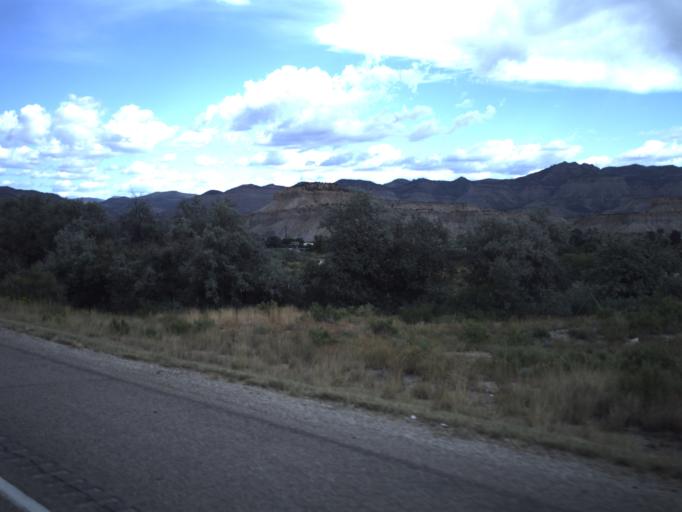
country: US
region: Utah
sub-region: Carbon County
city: Carbonville
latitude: 39.6225
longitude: -110.8572
